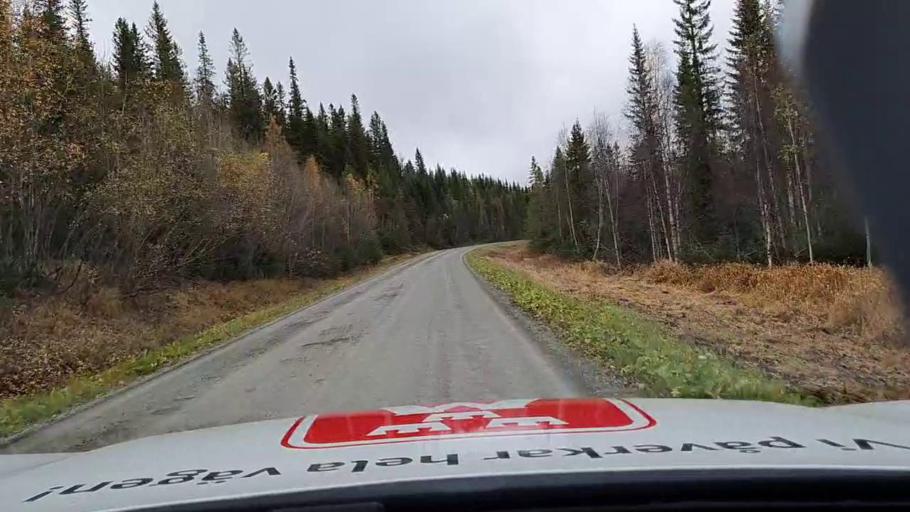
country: SE
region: Jaemtland
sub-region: Krokoms Kommun
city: Valla
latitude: 63.0432
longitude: 13.9611
